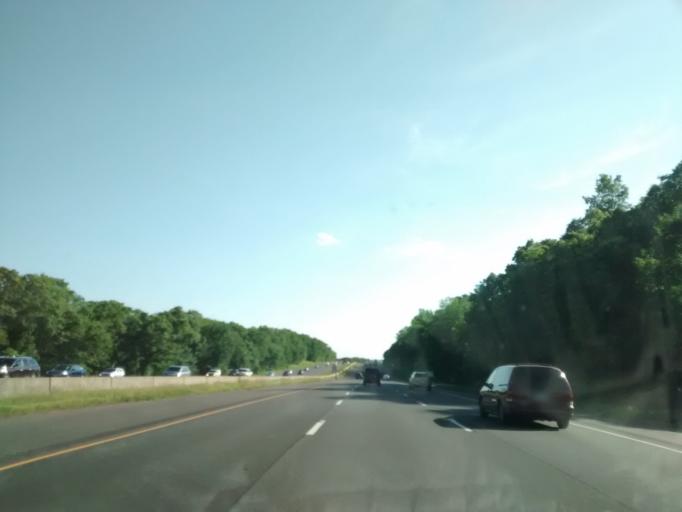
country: US
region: Connecticut
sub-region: Tolland County
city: Rockville
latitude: 41.8513
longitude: -72.4356
